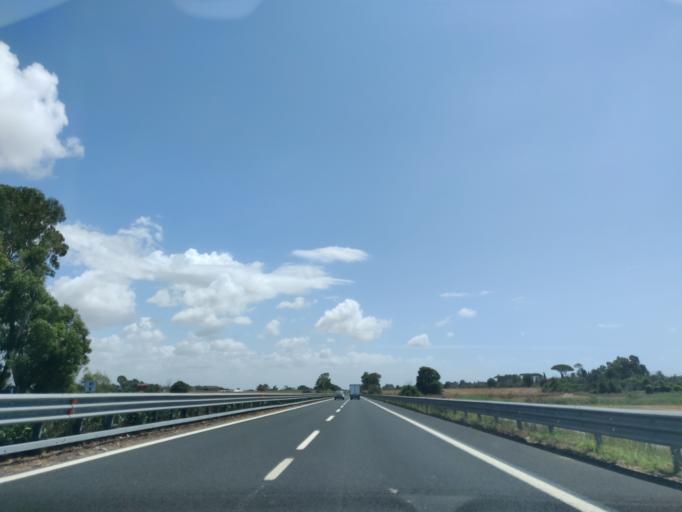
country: IT
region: Latium
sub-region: Citta metropolitana di Roma Capitale
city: Maccarese
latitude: 41.8499
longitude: 12.2683
